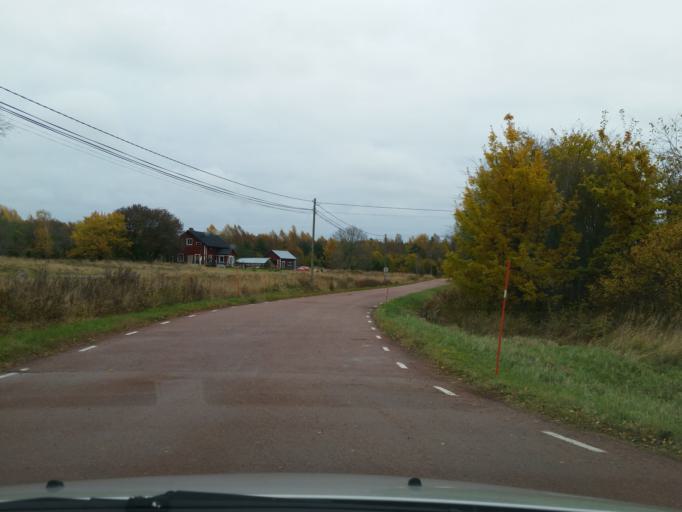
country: AX
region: Alands landsbygd
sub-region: Lemland
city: Lemland
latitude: 60.0260
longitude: 20.1690
